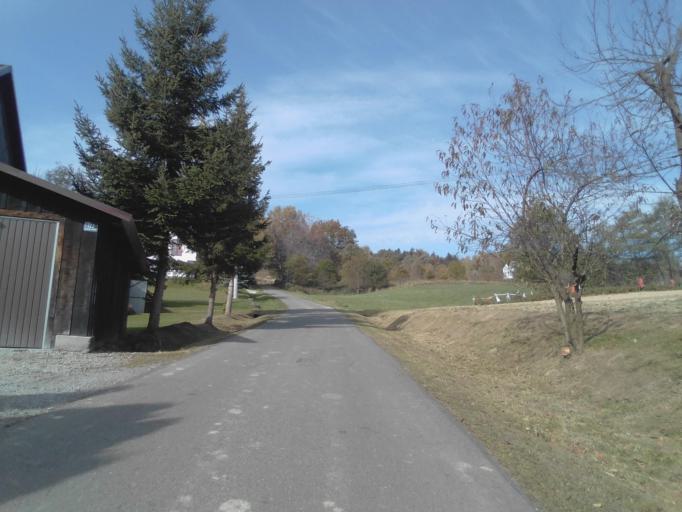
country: PL
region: Subcarpathian Voivodeship
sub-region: Powiat strzyzowski
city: Gwoznica Gorna
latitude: 49.8432
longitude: 21.9720
